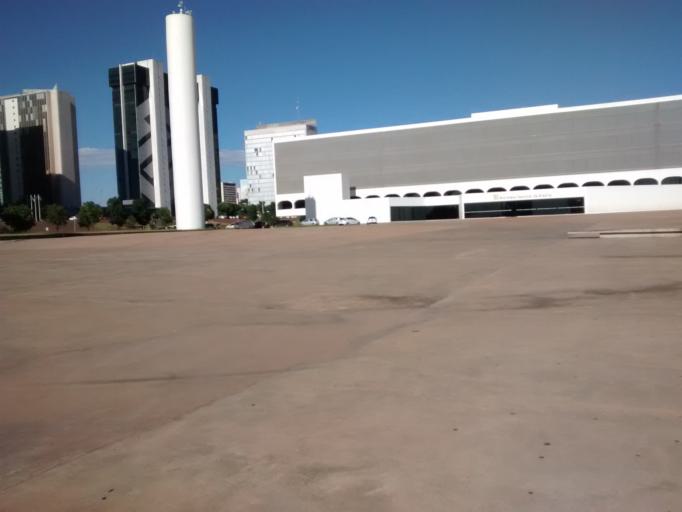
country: BR
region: Federal District
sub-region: Brasilia
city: Brasilia
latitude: -15.7969
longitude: -47.8788
